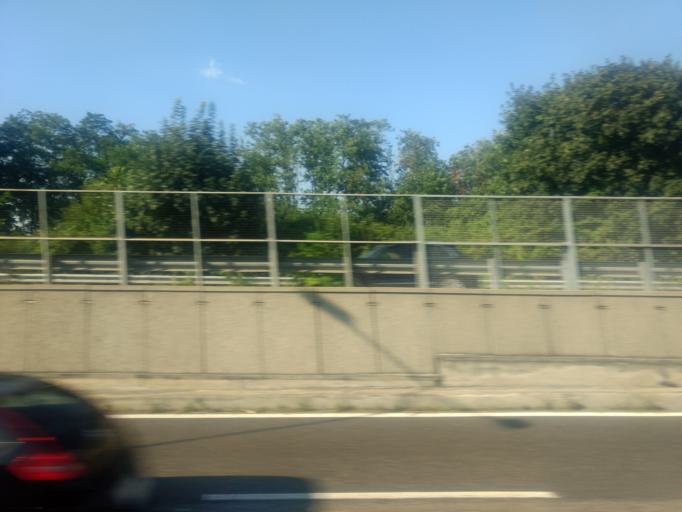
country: IT
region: Lombardy
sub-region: Provincia di Varese
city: Gallarate
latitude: 45.6425
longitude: 8.7966
